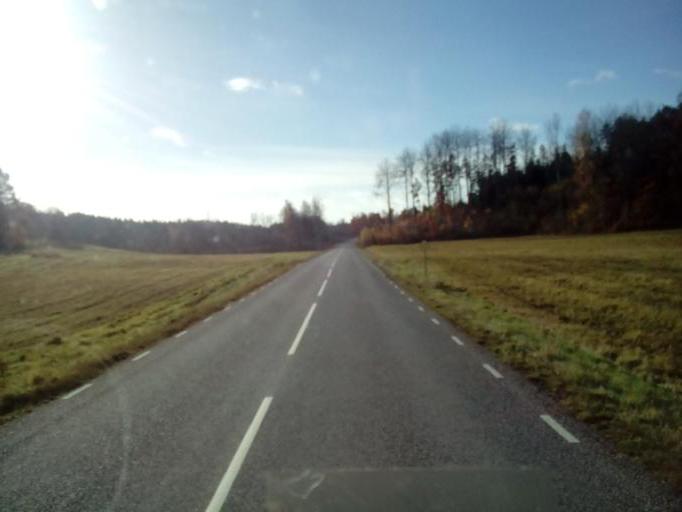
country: SE
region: Kalmar
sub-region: Vasterviks Kommun
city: Ankarsrum
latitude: 57.7817
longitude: 16.1651
